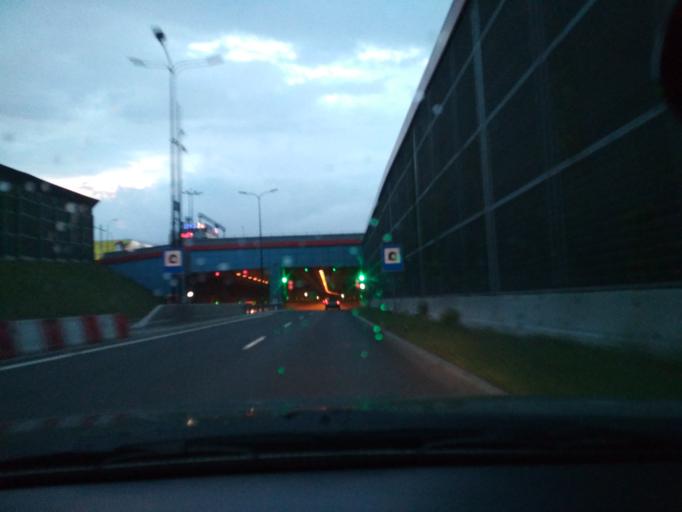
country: PL
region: Silesian Voivodeship
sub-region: Gliwice
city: Gliwice
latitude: 50.2968
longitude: 18.6777
